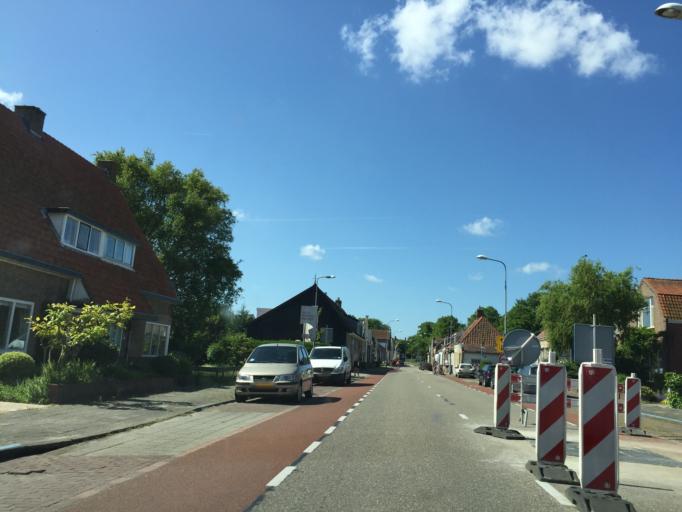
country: NL
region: Zeeland
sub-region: Gemeente Middelburg
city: Middelburg
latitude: 51.5048
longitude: 3.6259
